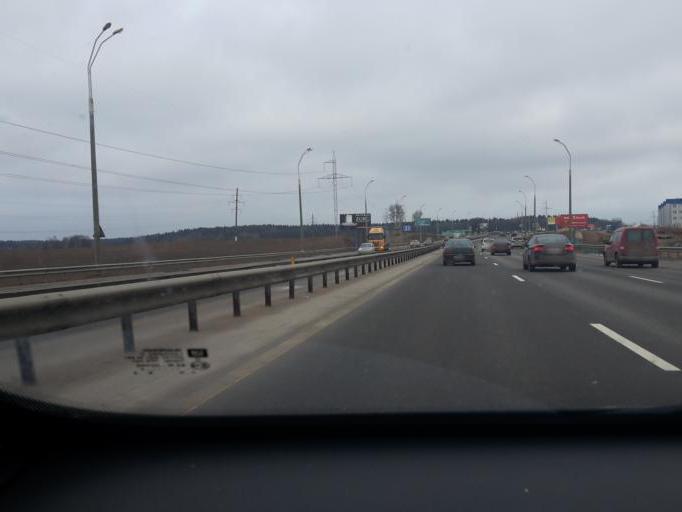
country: BY
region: Minsk
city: Novoye Medvezhino
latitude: 53.8975
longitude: 27.4093
